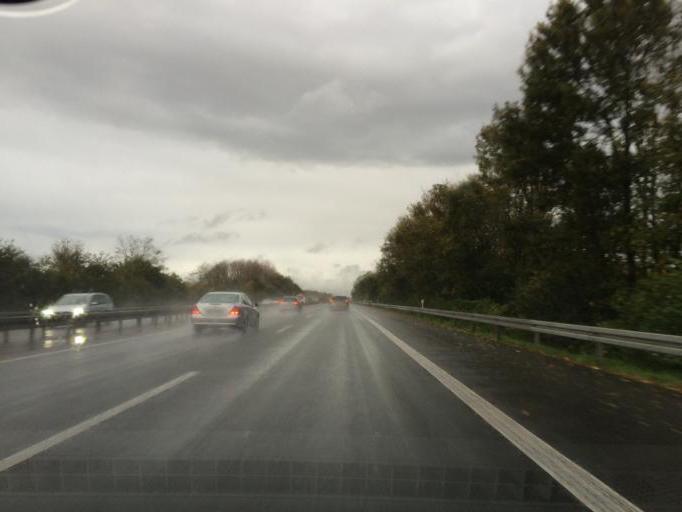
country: DE
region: North Rhine-Westphalia
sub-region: Regierungsbezirk Munster
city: Senden
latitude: 51.9036
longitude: 7.4403
